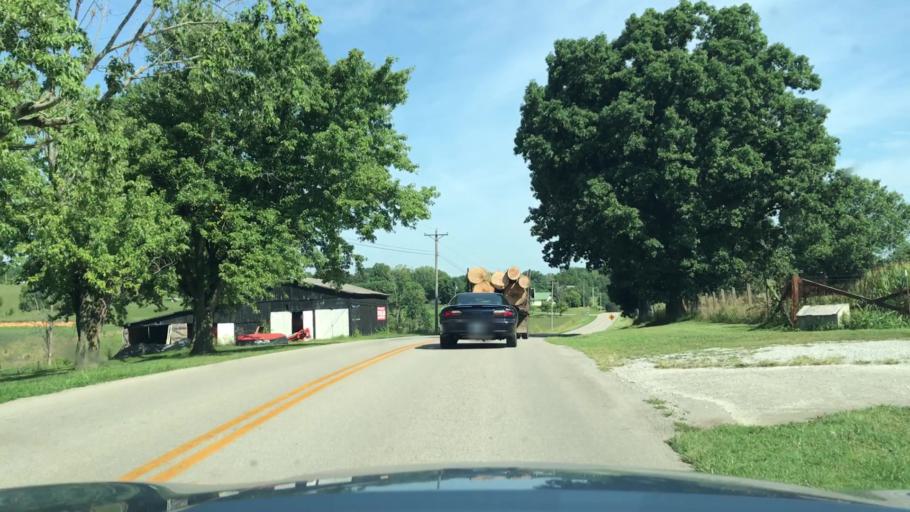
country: US
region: Kentucky
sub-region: Clinton County
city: Albany
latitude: 36.7538
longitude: -84.9957
